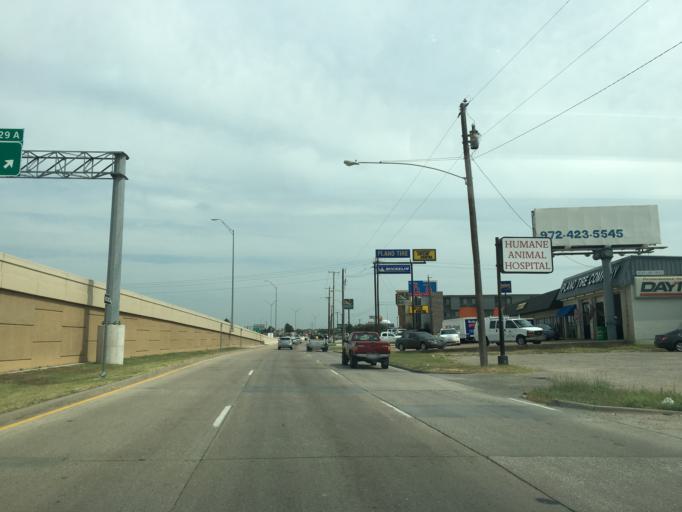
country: US
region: Texas
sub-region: Collin County
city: Plano
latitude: 33.0204
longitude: -96.7091
